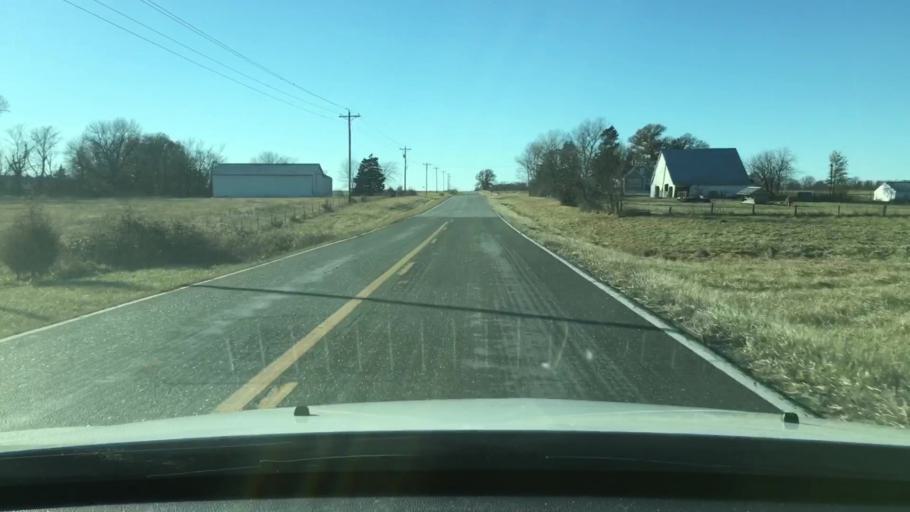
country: US
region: Missouri
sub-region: Audrain County
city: Mexico
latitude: 39.2764
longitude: -91.7927
